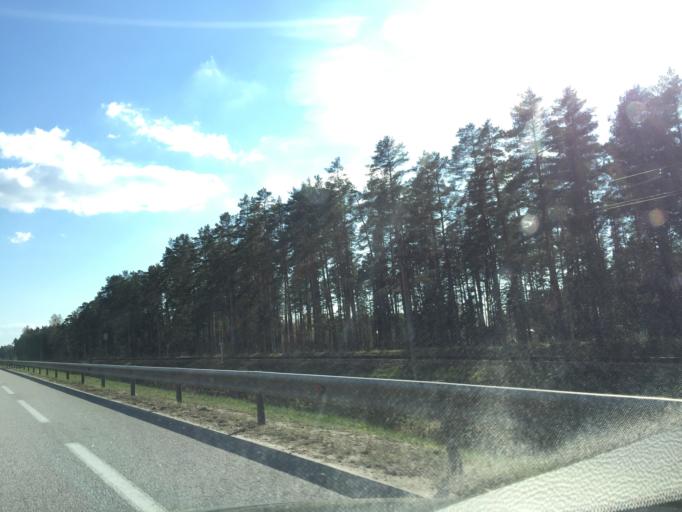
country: LV
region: Saulkrastu
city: Saulkrasti
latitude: 57.3165
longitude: 24.4480
